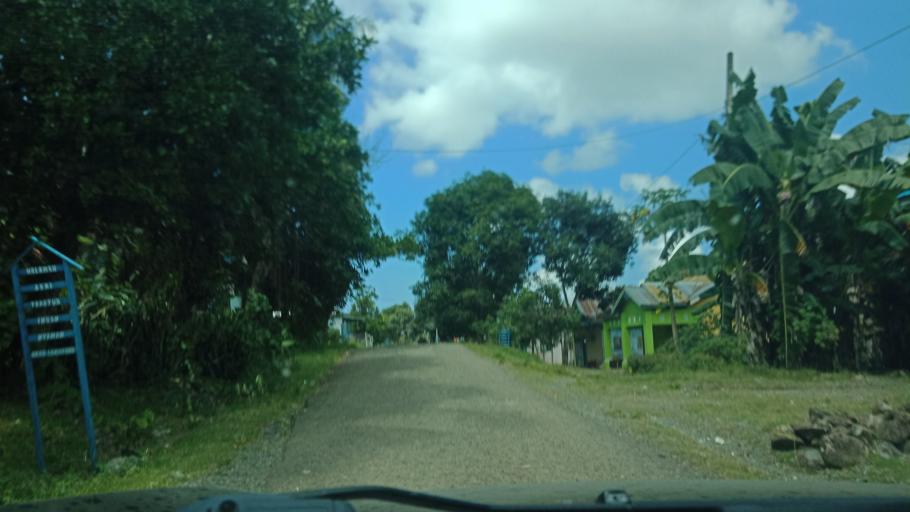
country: ID
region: South Sulawesi
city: Kadai
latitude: -4.7728
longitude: 120.3365
